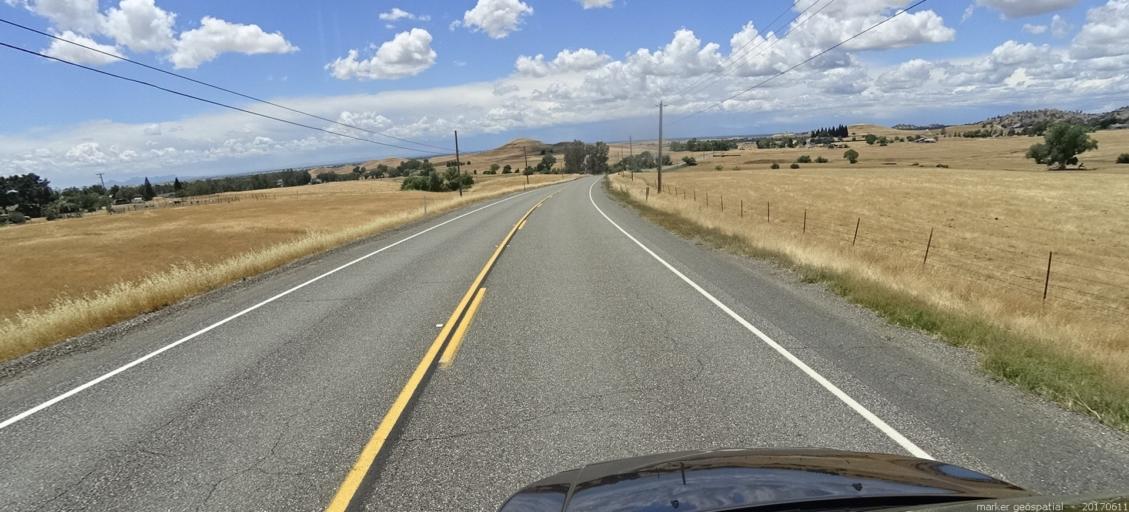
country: US
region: California
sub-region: Butte County
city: Paradise
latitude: 39.6487
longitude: -121.6043
